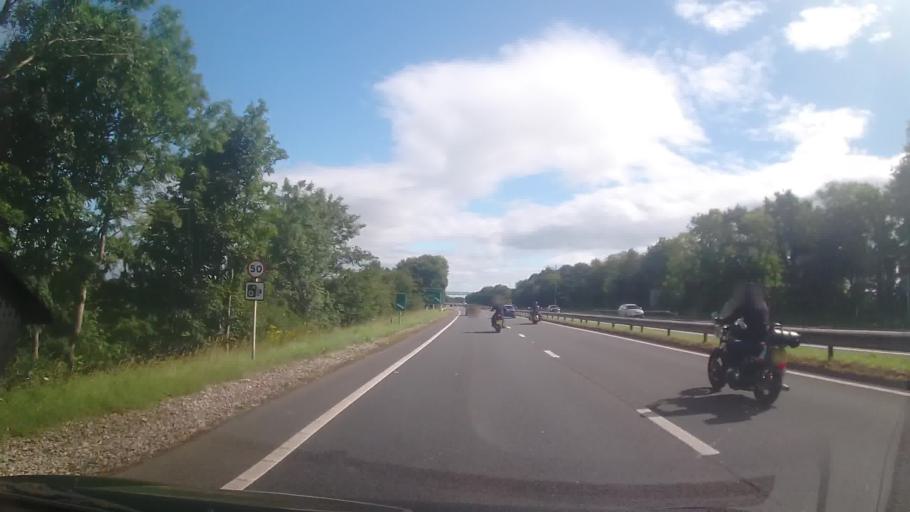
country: GB
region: Wales
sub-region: Wrexham
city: Wrexham
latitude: 53.0680
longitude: -2.9969
